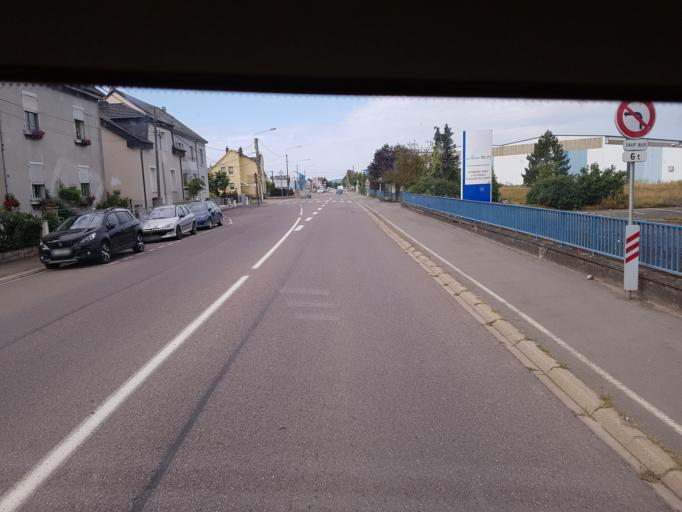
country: FR
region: Lorraine
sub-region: Departement de la Moselle
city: Yutz
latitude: 49.3663
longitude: 6.2065
